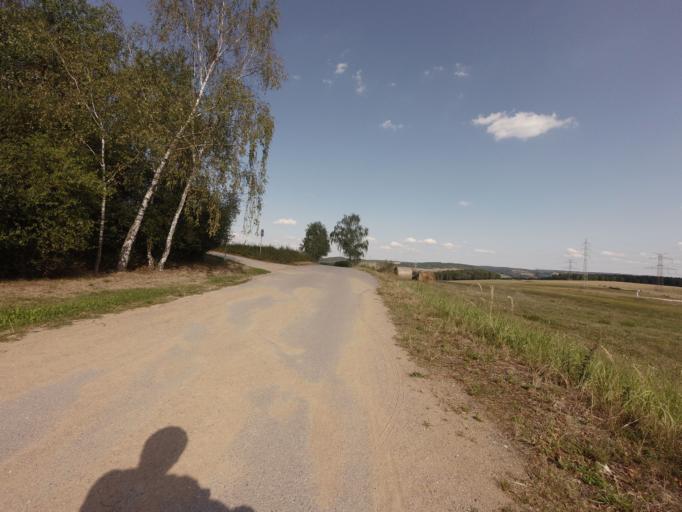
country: CZ
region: Jihocesky
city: Tyn nad Vltavou
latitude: 49.1739
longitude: 14.4264
